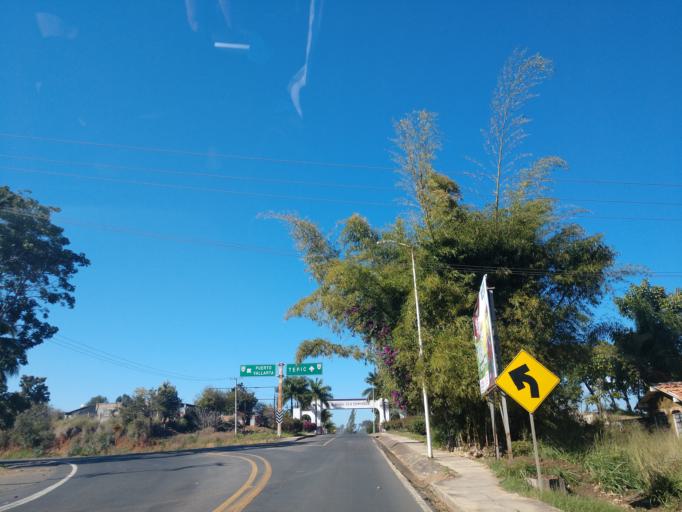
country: MX
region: Nayarit
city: Compostela
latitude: 21.2484
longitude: -104.9012
